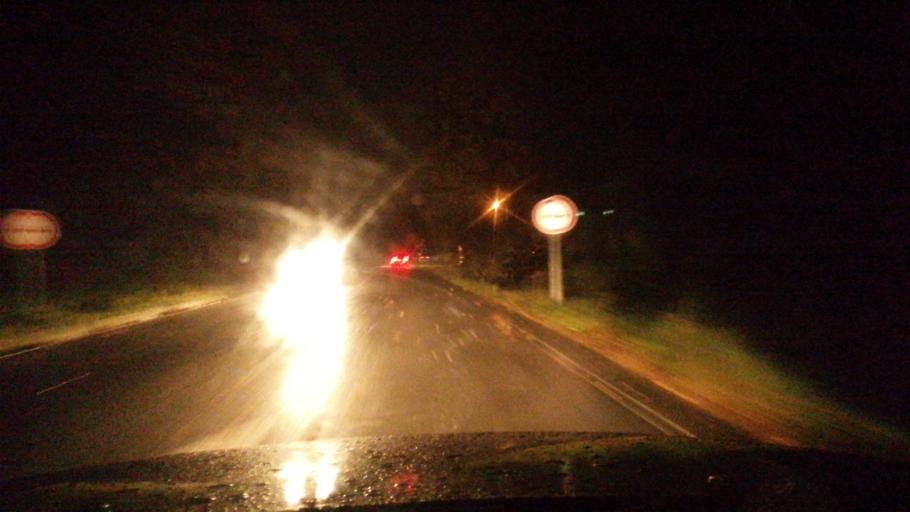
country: PT
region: Viseu
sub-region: Moimenta da Beira
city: Moimenta da Beira
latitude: 40.9626
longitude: -7.5960
